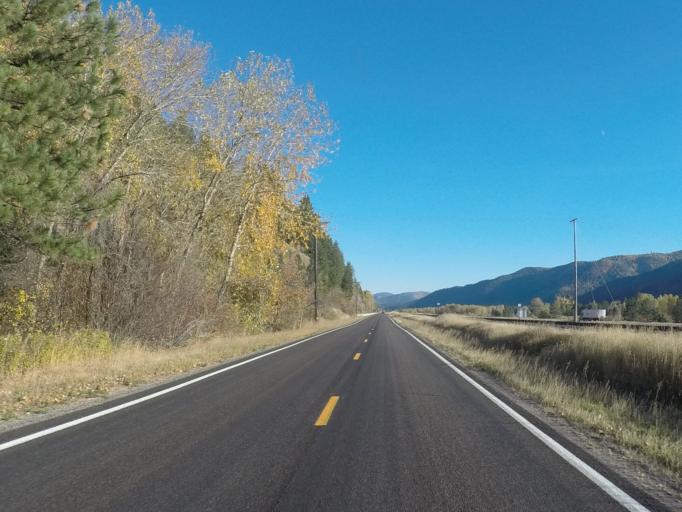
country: US
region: Montana
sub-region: Missoula County
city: Bonner-West Riverside
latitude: 46.8264
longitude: -113.8102
